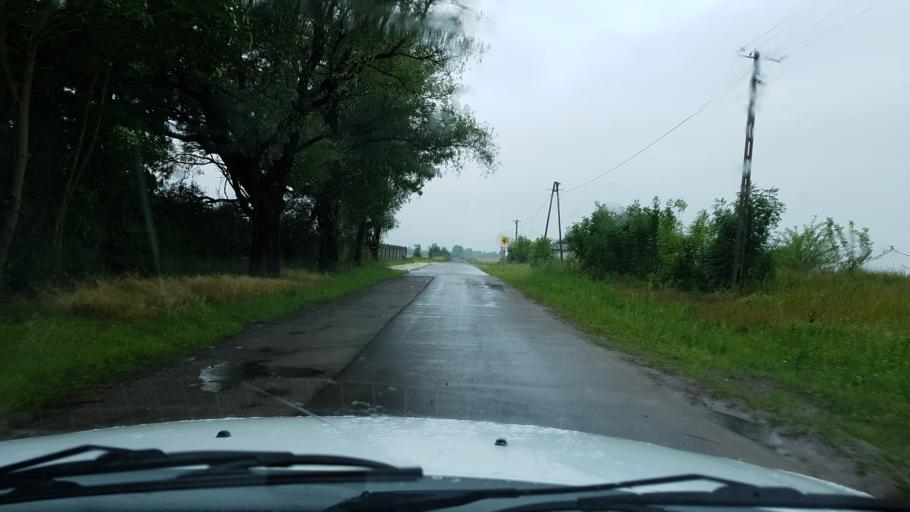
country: PL
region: West Pomeranian Voivodeship
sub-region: Powiat kolobrzeski
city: Ustronie Morskie
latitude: 54.2137
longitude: 15.8472
